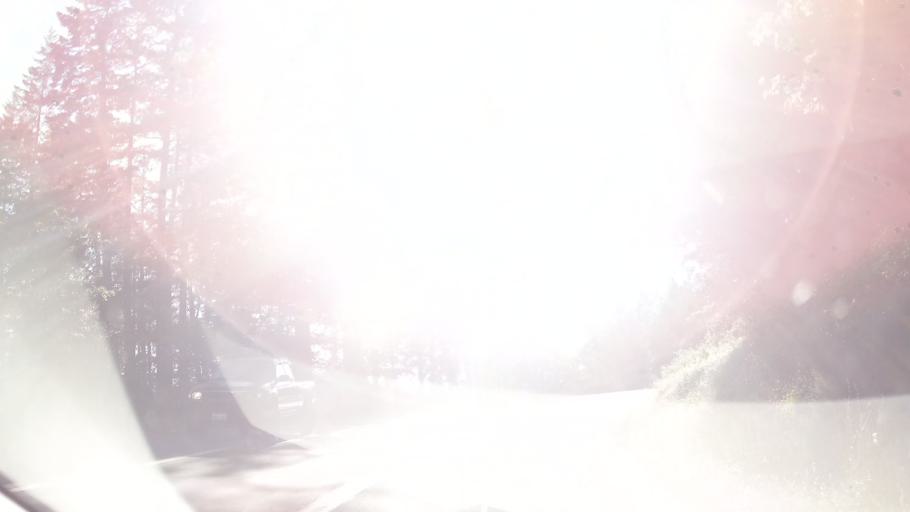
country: US
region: California
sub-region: Mendocino County
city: Brooktrails
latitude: 39.3884
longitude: -123.4418
